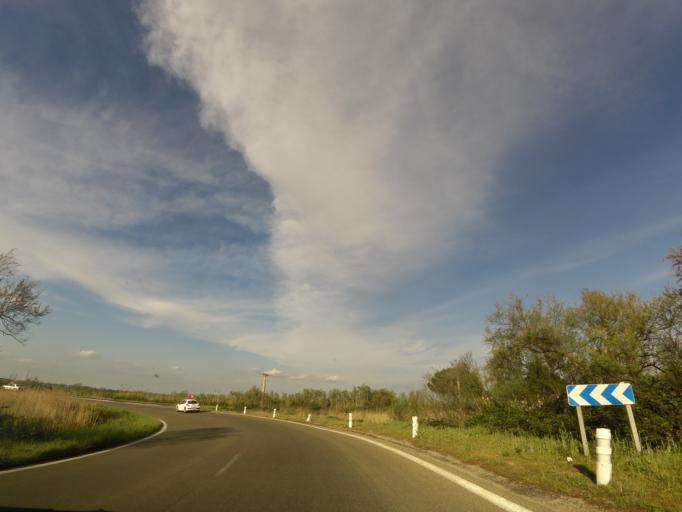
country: FR
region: Languedoc-Roussillon
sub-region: Departement de l'Herault
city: La Grande-Motte
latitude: 43.5756
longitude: 4.1034
